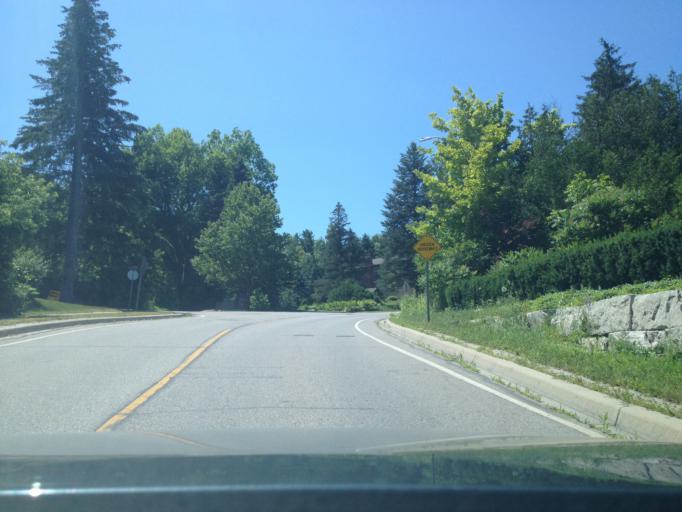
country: CA
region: Ontario
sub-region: Halton
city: Milton
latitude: 43.6642
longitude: -79.9286
